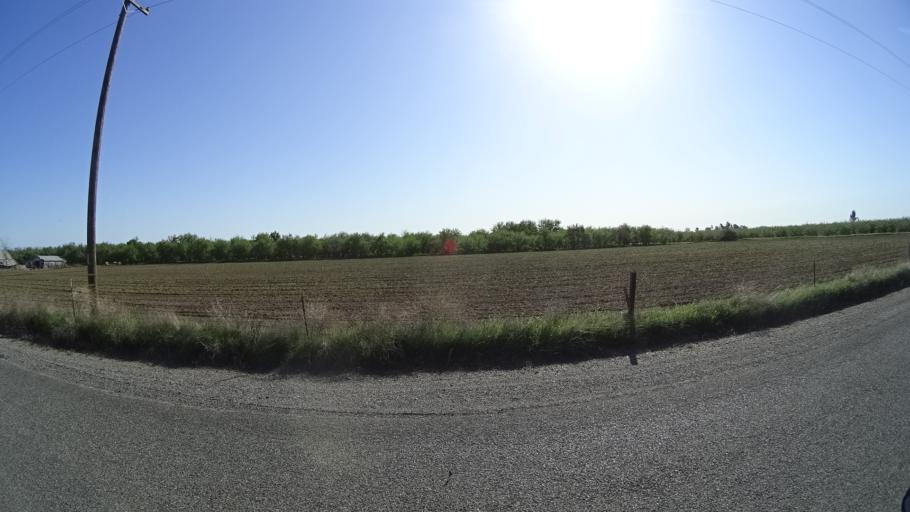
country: US
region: California
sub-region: Glenn County
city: Hamilton City
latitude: 39.7941
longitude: -122.0854
